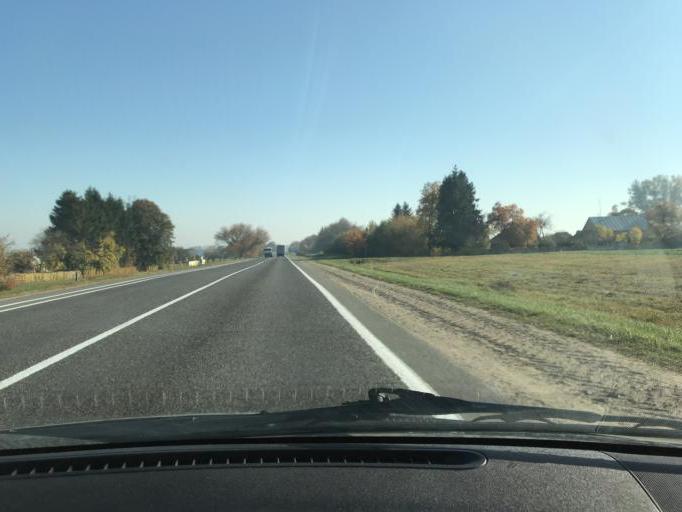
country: BY
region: Minsk
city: Klyetsk
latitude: 52.9702
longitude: 26.6475
